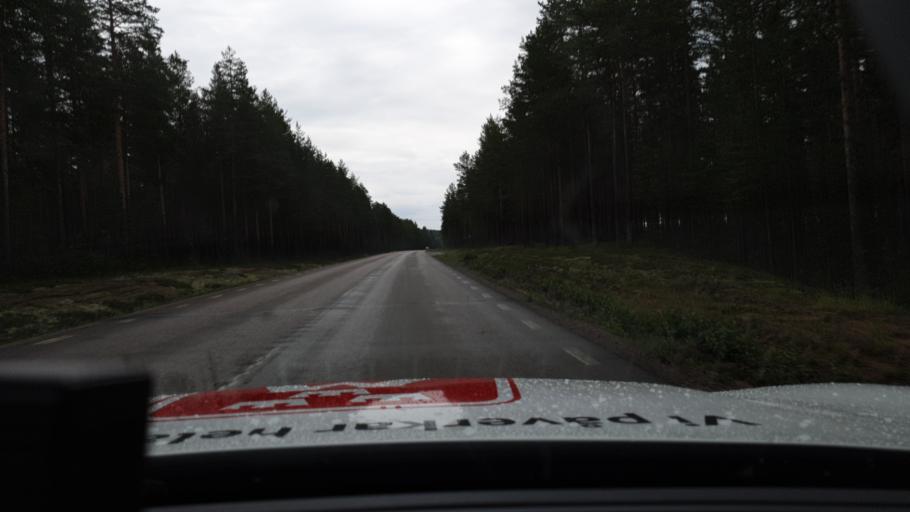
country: SE
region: Norrbotten
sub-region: Alvsbyns Kommun
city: AElvsbyn
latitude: 66.1381
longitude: 20.8906
